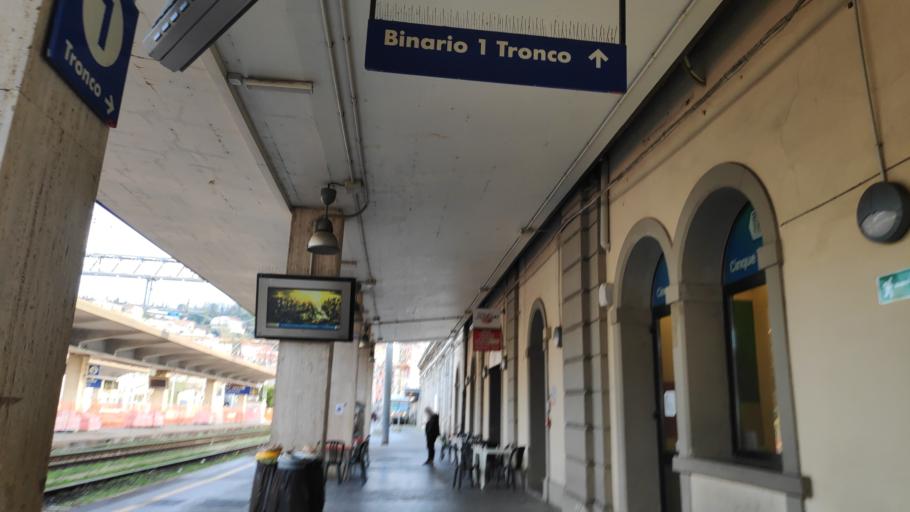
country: IT
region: Liguria
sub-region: Provincia di La Spezia
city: La Spezia
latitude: 44.1115
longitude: 9.8143
